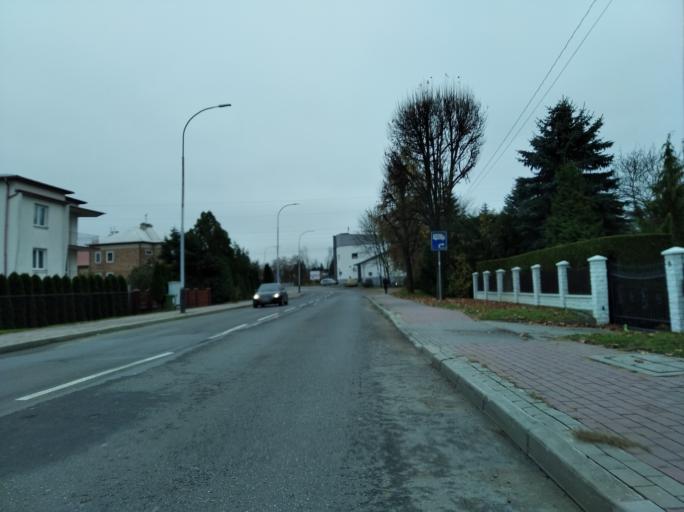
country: PL
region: Subcarpathian Voivodeship
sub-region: Krosno
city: Krosno
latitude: 49.6980
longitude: 21.7627
